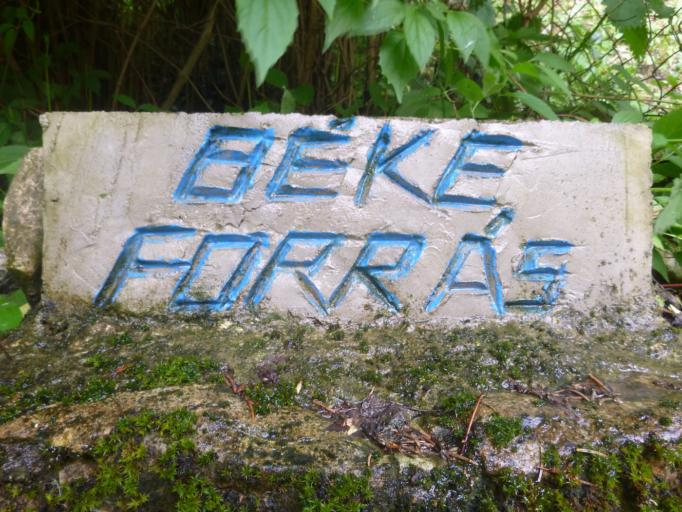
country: HU
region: Baranya
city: Hosszuheteny
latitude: 46.2101
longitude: 18.3759
